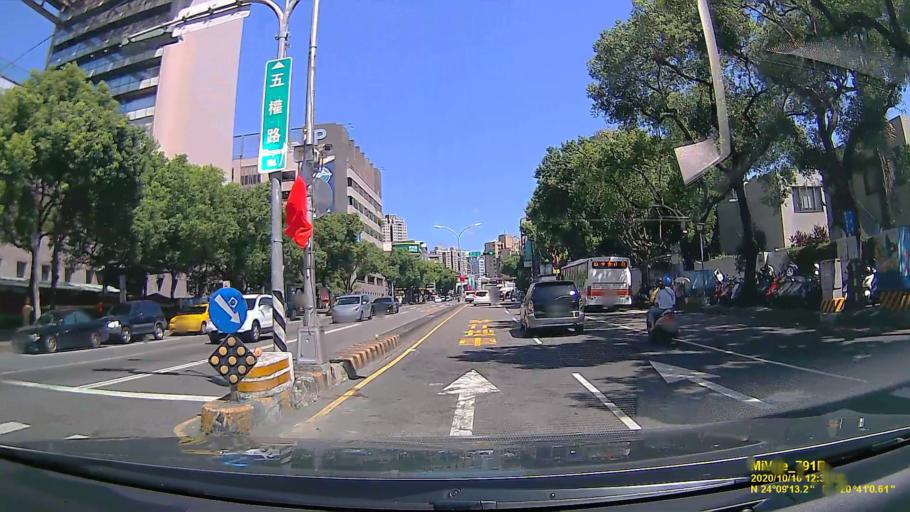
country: TW
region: Taiwan
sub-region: Taichung City
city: Taichung
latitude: 24.1536
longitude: 120.6836
